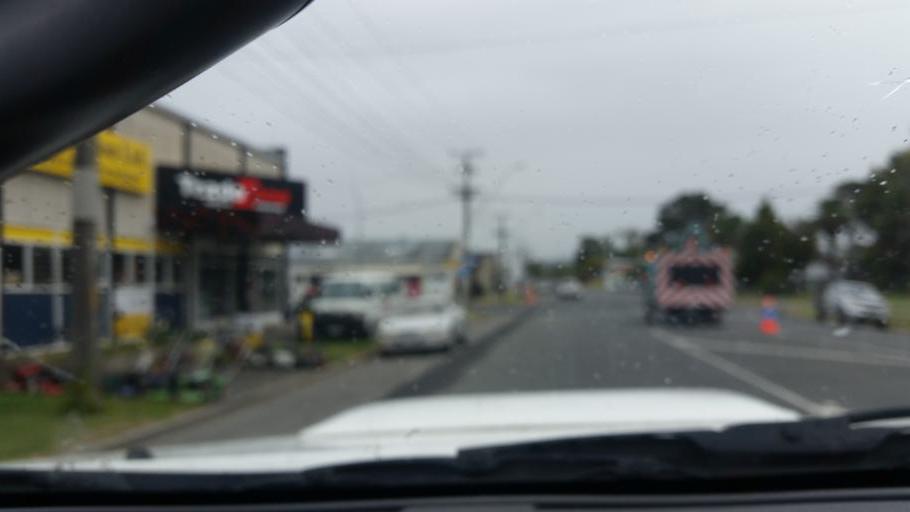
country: NZ
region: Northland
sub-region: Kaipara District
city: Dargaville
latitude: -35.9381
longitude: 173.8723
